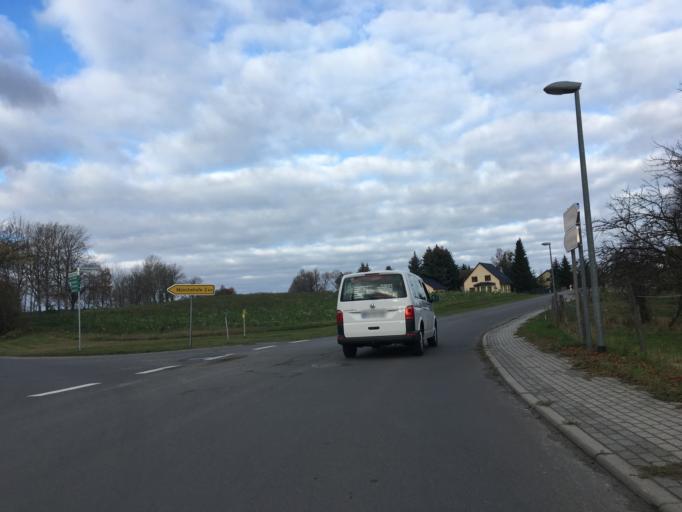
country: DE
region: Brandenburg
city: Muncheberg
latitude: 52.5449
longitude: 14.1659
